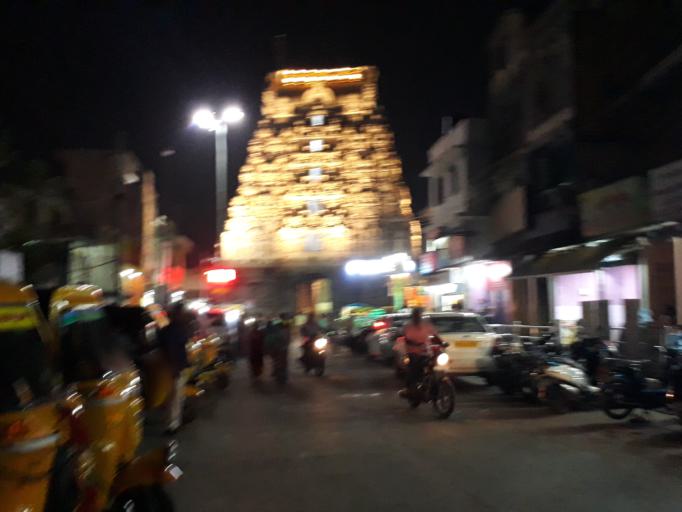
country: IN
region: Tamil Nadu
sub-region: Kancheepuram
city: Kanchipuram
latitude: 12.8401
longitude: 79.7041
